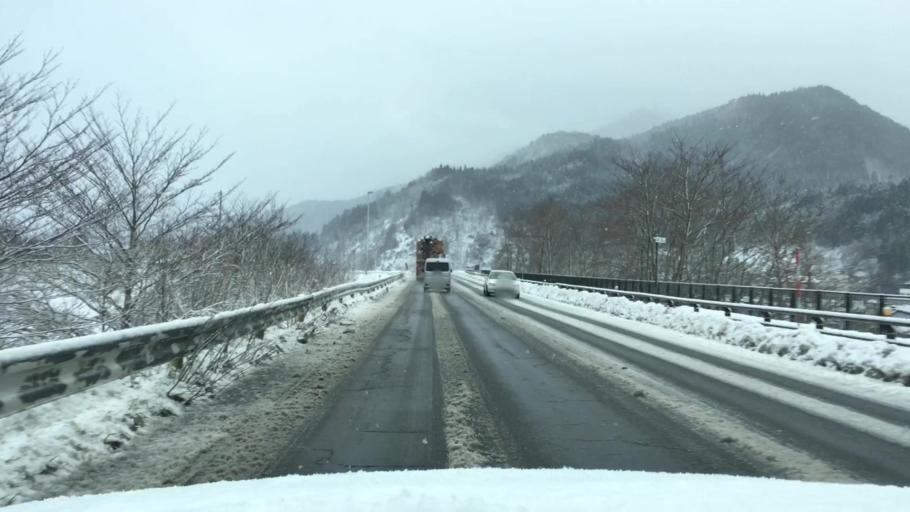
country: JP
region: Aomori
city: Kuroishi
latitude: 40.5234
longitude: 140.5813
